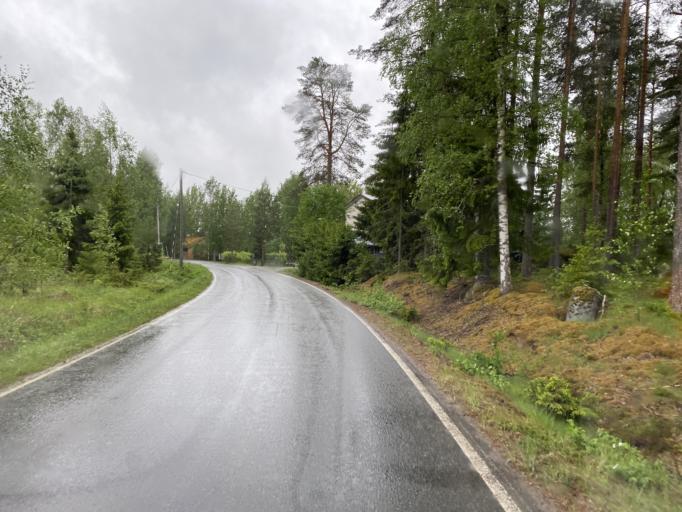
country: FI
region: Haeme
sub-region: Forssa
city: Humppila
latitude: 61.0678
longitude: 23.3189
